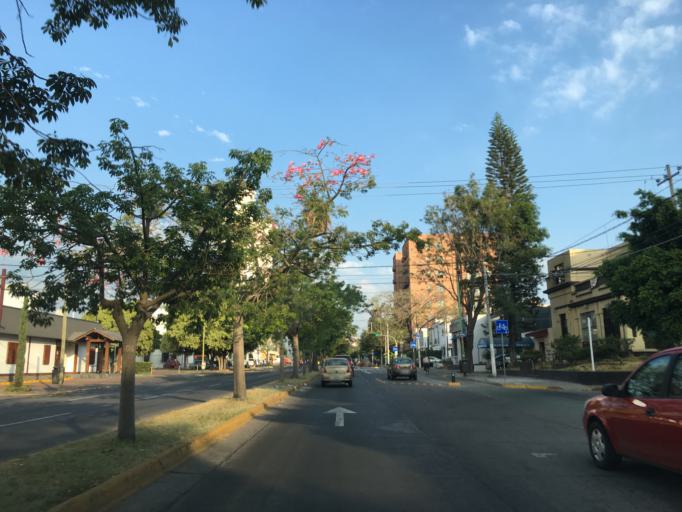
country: MX
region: Jalisco
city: Guadalajara
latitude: 20.6709
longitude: -103.3624
